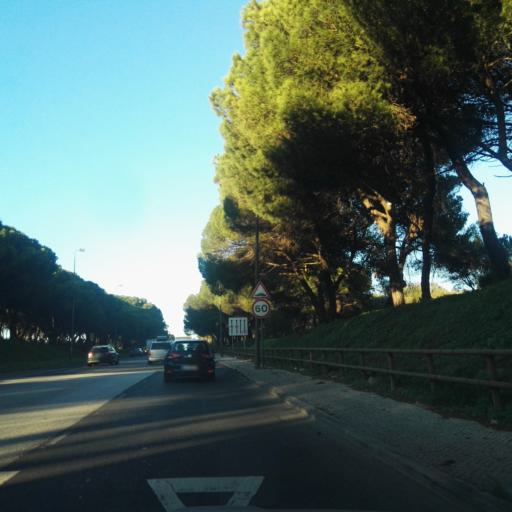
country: PT
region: Lisbon
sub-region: Loures
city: Moscavide
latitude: 38.7732
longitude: -9.1234
